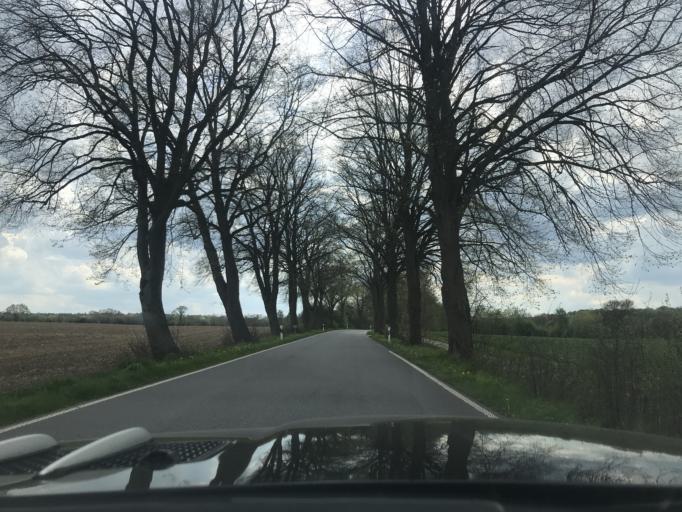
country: DE
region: Schleswig-Holstein
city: Timmendorfer Strand
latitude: 53.9427
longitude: 10.7884
